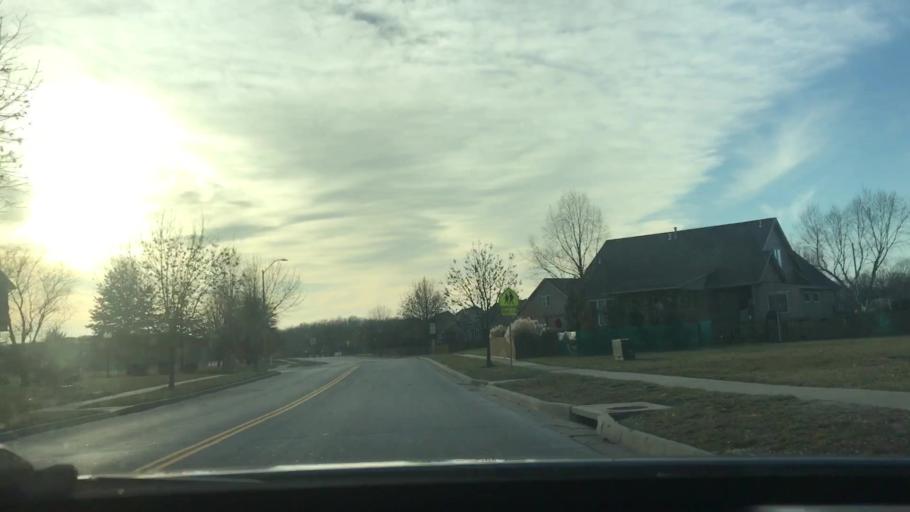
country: US
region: Missouri
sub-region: Jackson County
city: East Independence
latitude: 39.0188
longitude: -94.3701
